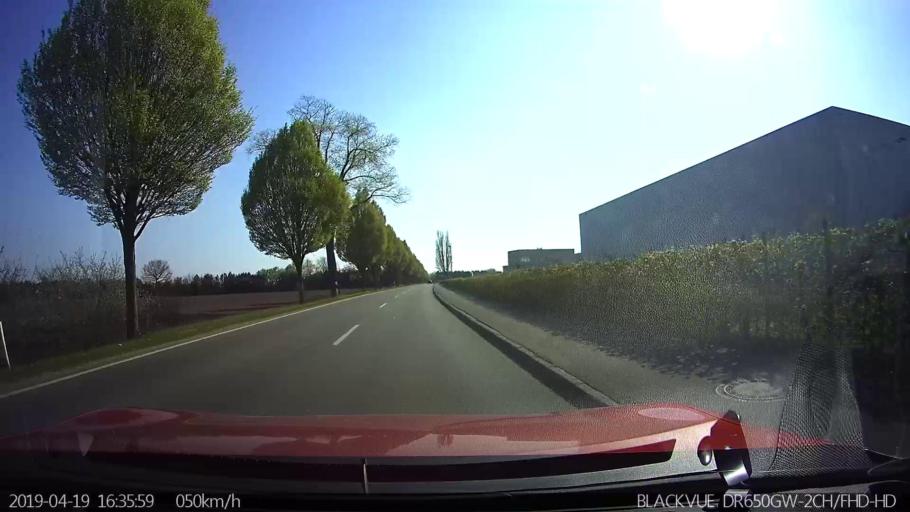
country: DE
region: Schleswig-Holstein
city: Tangstedt
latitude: 53.6680
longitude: 9.8401
